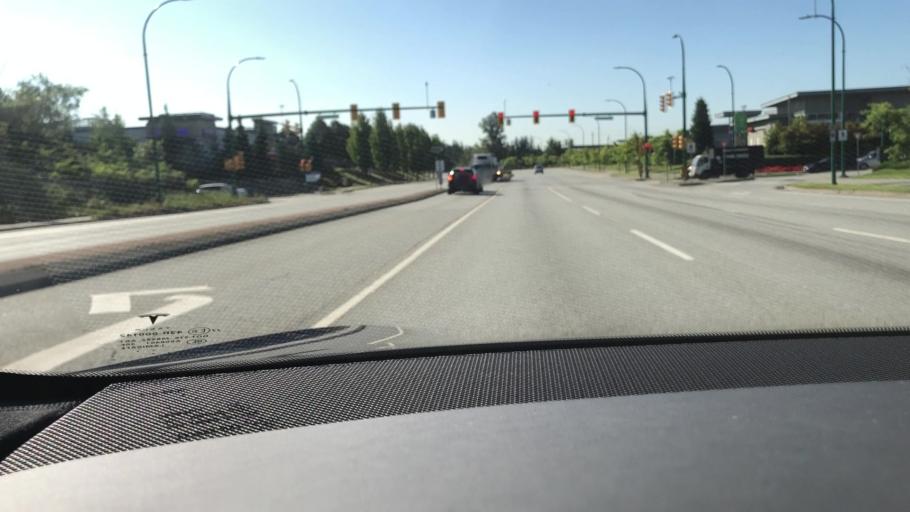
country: CA
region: British Columbia
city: New Westminster
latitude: 49.2002
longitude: -122.9798
